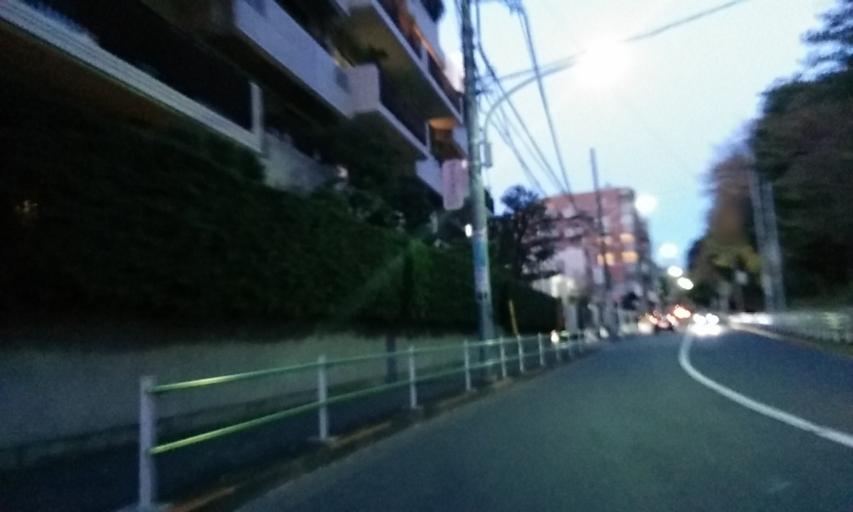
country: JP
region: Tokyo
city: Tokyo
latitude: 35.6522
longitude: 139.7241
